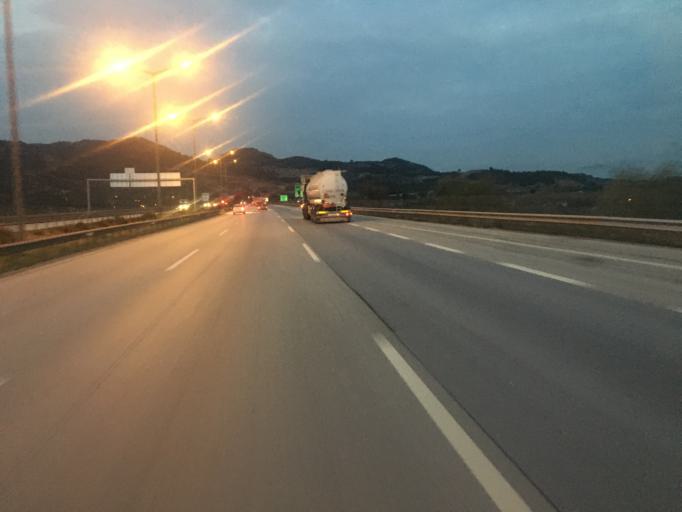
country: TR
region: Osmaniye
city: Haruniye
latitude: 37.1947
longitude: 36.4225
